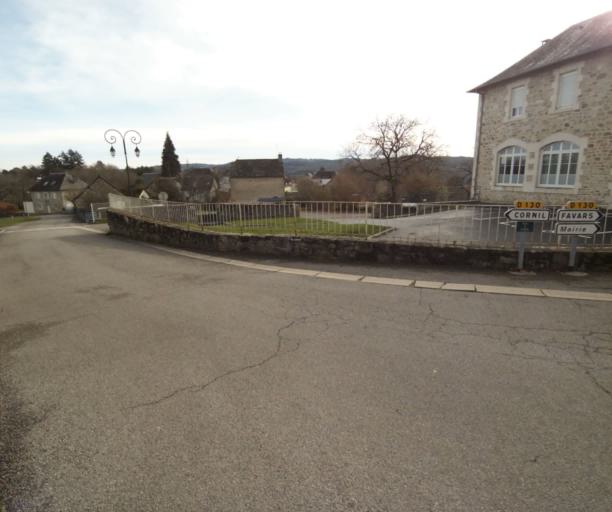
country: FR
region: Limousin
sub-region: Departement de la Correze
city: Chameyrat
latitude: 45.2340
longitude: 1.6985
